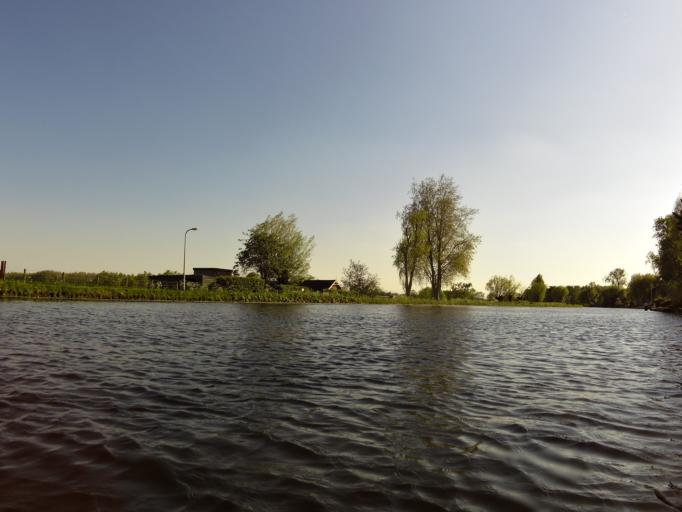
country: NL
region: South Holland
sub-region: Gemeente Voorschoten
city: Voorschoten
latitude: 52.0952
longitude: 4.4152
